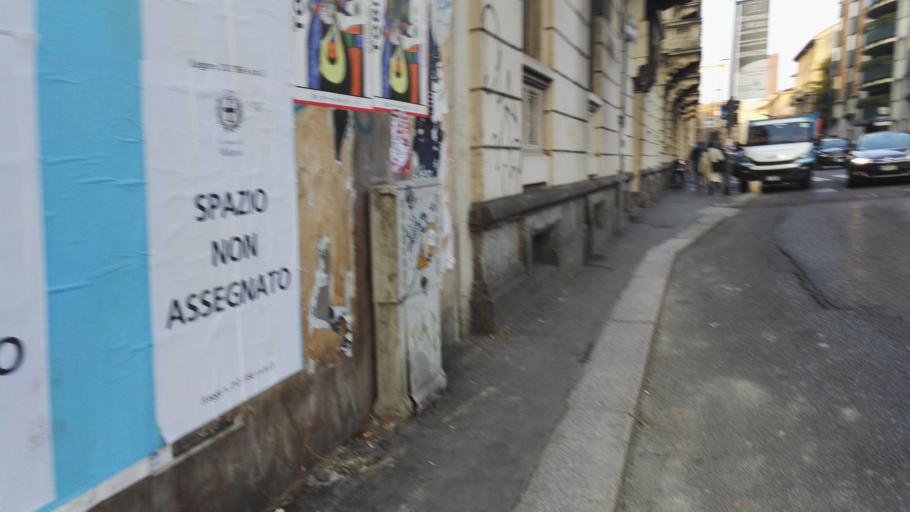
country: IT
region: Lombardy
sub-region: Citta metropolitana di Milano
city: Milano
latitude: 45.4838
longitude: 9.1845
